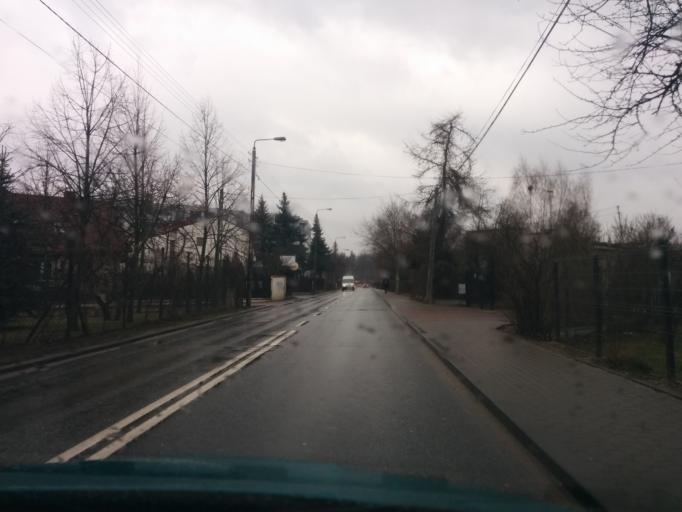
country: PL
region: Masovian Voivodeship
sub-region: Warszawa
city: Bialoleka
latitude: 52.3375
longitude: 20.9380
